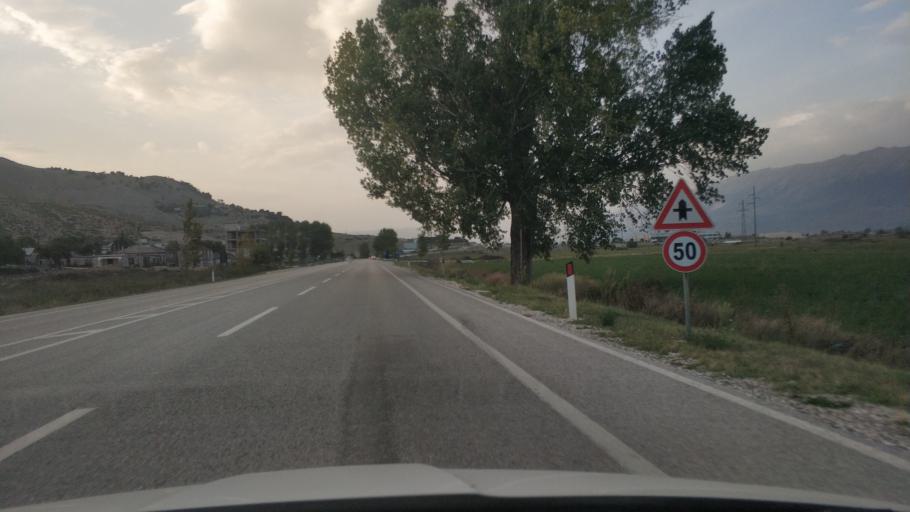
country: AL
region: Gjirokaster
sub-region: Rrethi i Gjirokastres
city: Libohove
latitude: 39.9660
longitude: 20.2405
